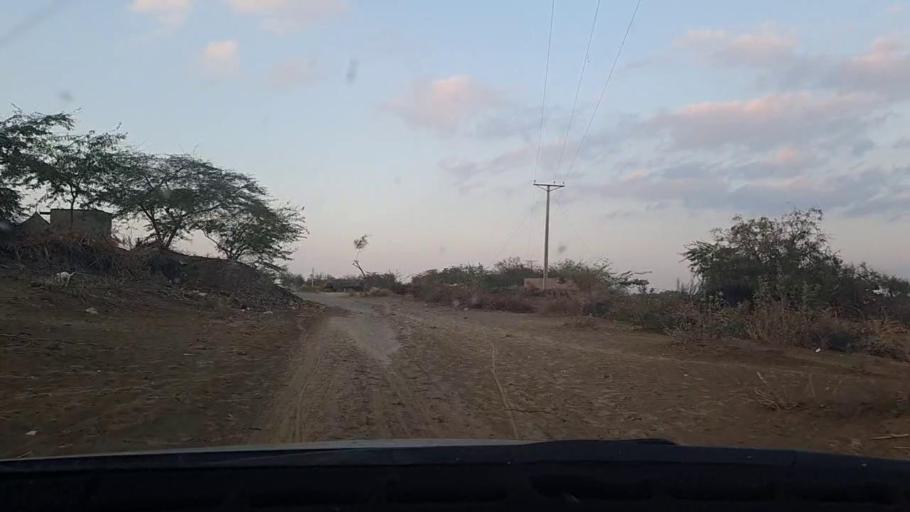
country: PK
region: Sindh
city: Tando Mittha Khan
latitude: 25.9550
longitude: 69.3426
